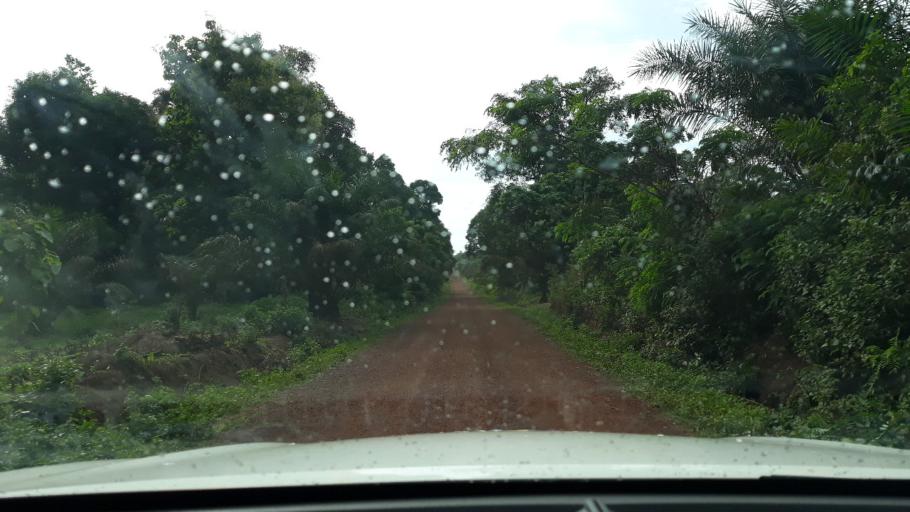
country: CD
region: Equateur
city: Libenge
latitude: 3.7250
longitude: 18.7646
